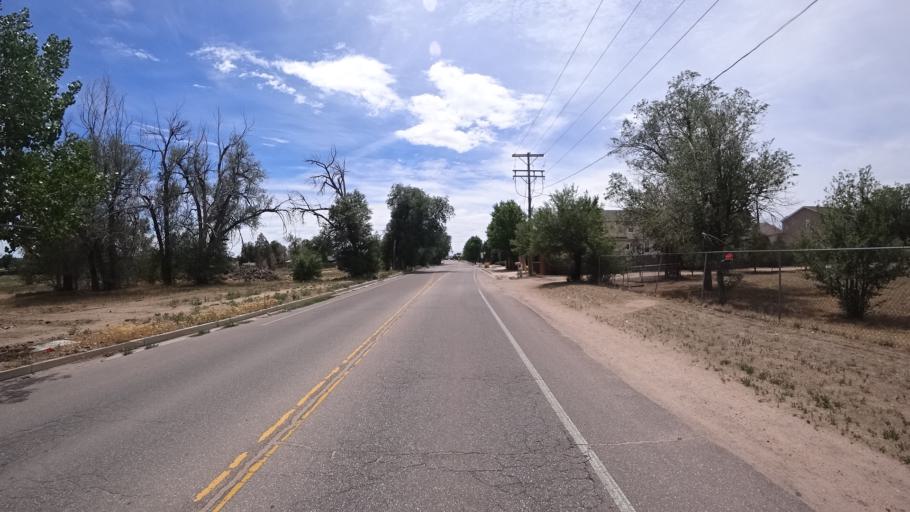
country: US
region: Colorado
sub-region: El Paso County
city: Fountain
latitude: 38.6792
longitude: -104.6875
